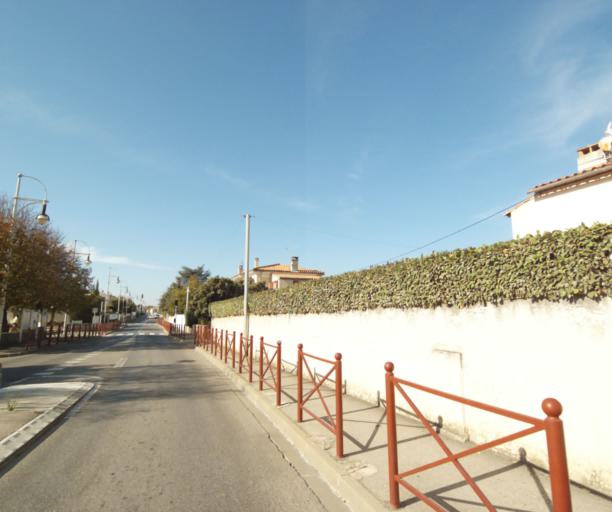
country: FR
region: Provence-Alpes-Cote d'Azur
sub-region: Departement des Bouches-du-Rhone
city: Chateauneuf-les-Martigues
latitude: 43.3962
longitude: 5.1182
